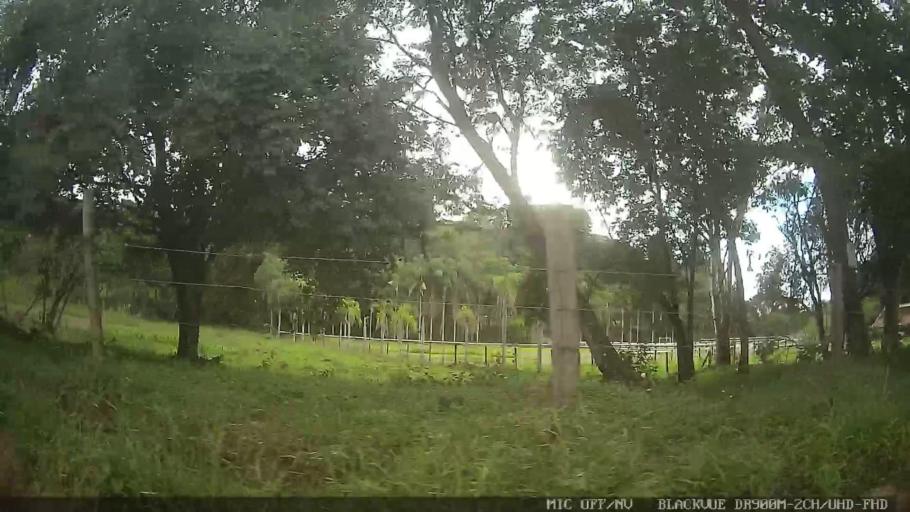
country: BR
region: Sao Paulo
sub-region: Bom Jesus Dos Perdoes
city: Bom Jesus dos Perdoes
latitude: -23.1254
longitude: -46.4949
